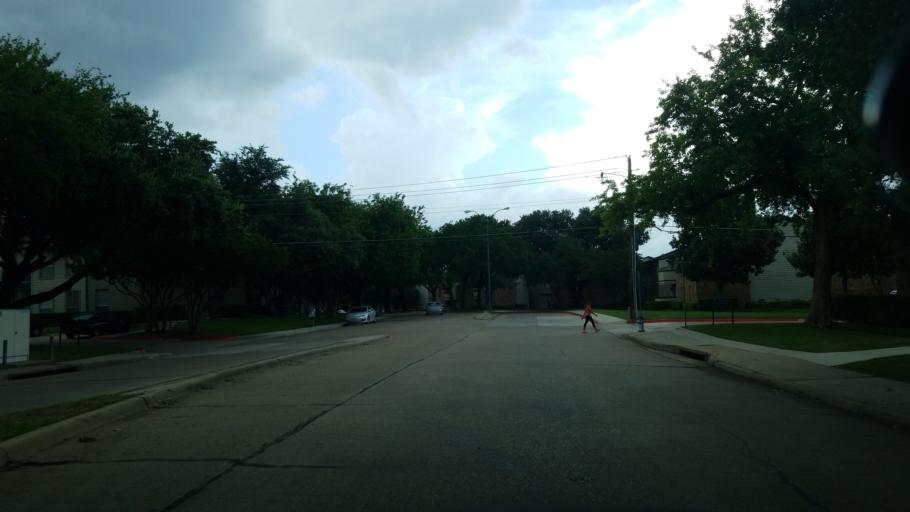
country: US
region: Texas
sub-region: Dallas County
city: Highland Park
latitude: 32.8558
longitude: -96.7654
